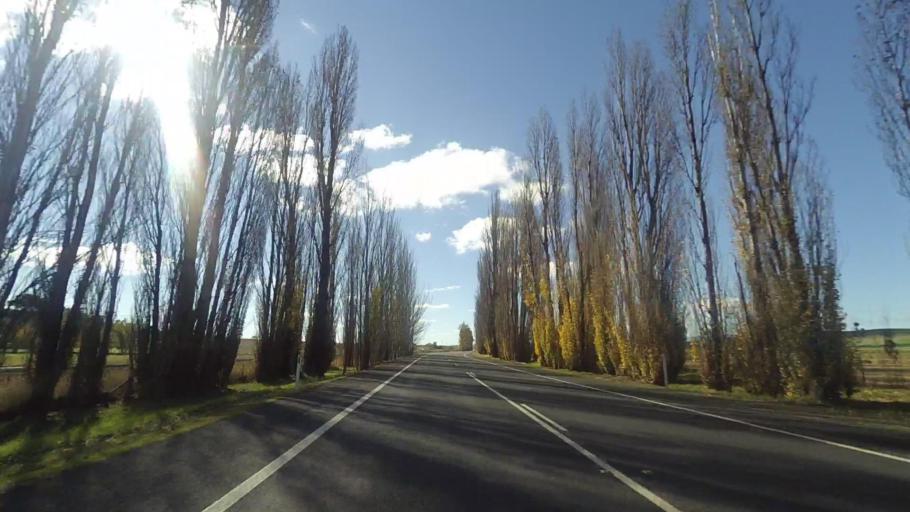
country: AU
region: New South Wales
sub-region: Bathurst Regional
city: Perthville
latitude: -33.4604
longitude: 149.5728
